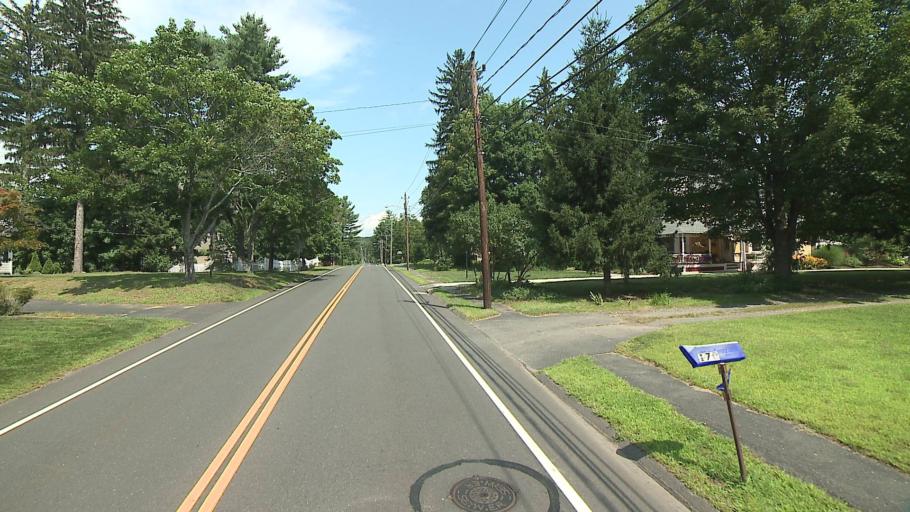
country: US
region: Connecticut
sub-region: Hartford County
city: Collinsville
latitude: 41.7638
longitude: -72.8891
